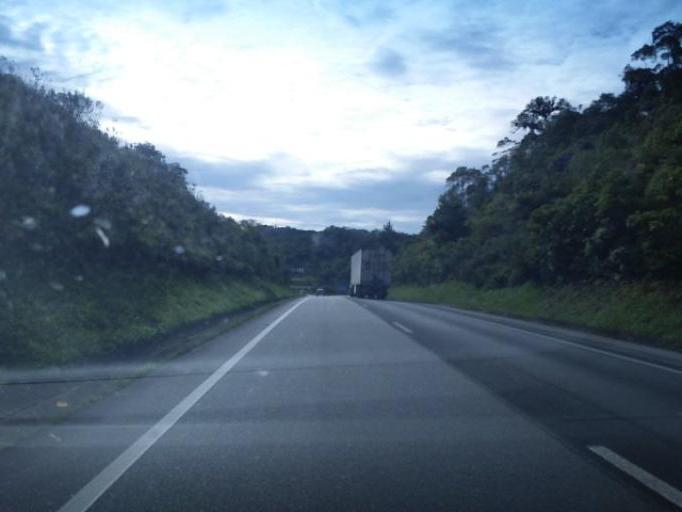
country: BR
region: Parana
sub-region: Antonina
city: Antonina
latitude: -25.1070
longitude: -48.7843
